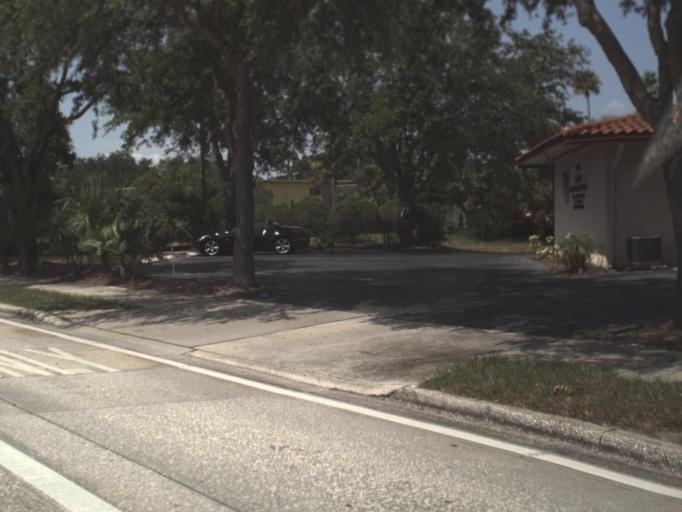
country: US
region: Florida
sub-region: Pinellas County
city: Gulfport
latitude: 27.7779
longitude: -82.7144
